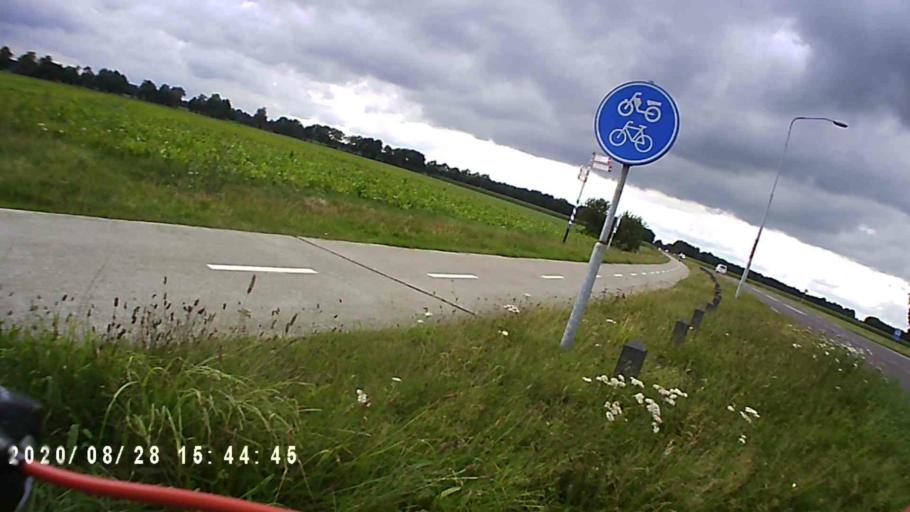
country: NL
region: Drenthe
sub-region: Gemeente Tynaarlo
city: Vries
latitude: 53.1009
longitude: 6.5426
